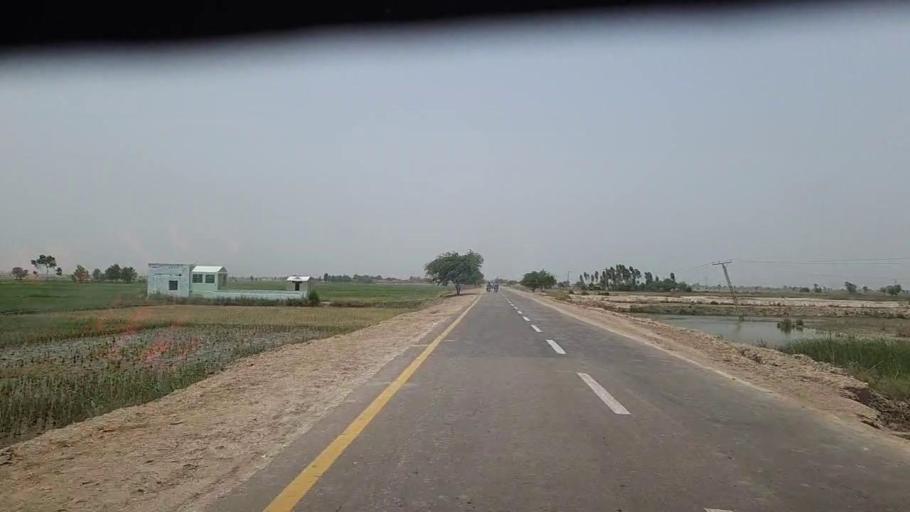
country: PK
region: Sindh
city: Sita Road
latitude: 27.0402
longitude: 67.8913
